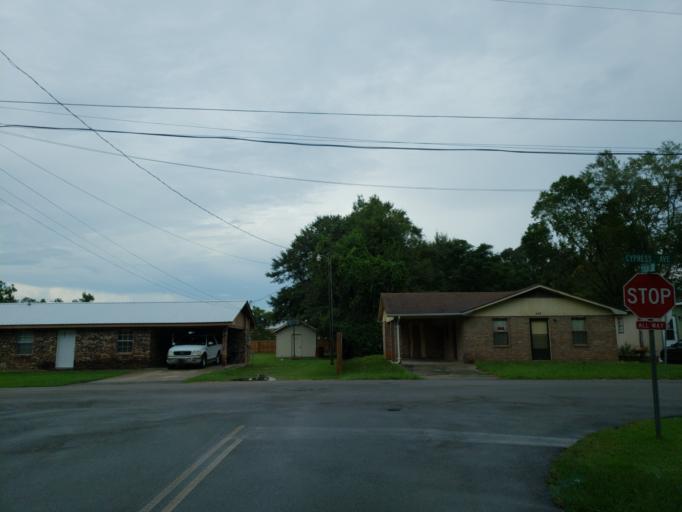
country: US
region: Mississippi
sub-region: Forrest County
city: Hattiesburg
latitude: 31.3100
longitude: -89.2941
